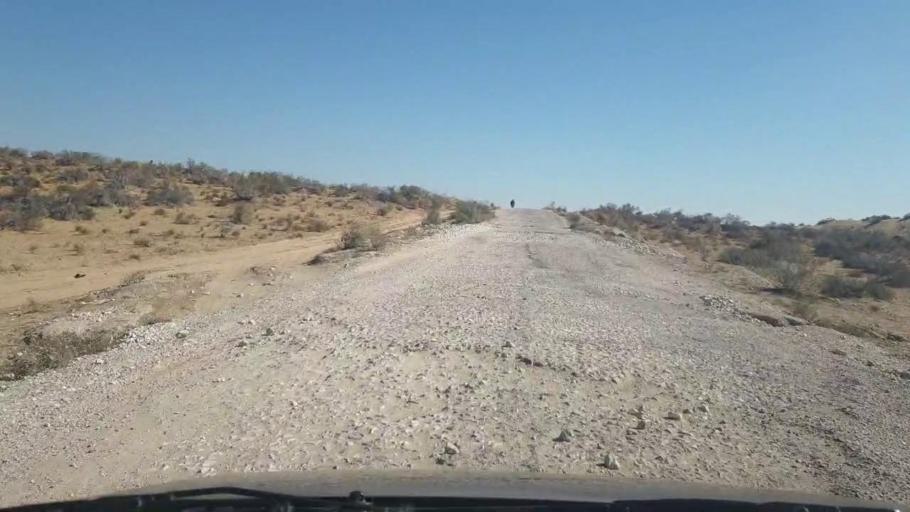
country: PK
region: Sindh
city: Bozdar
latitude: 27.0000
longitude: 68.8515
